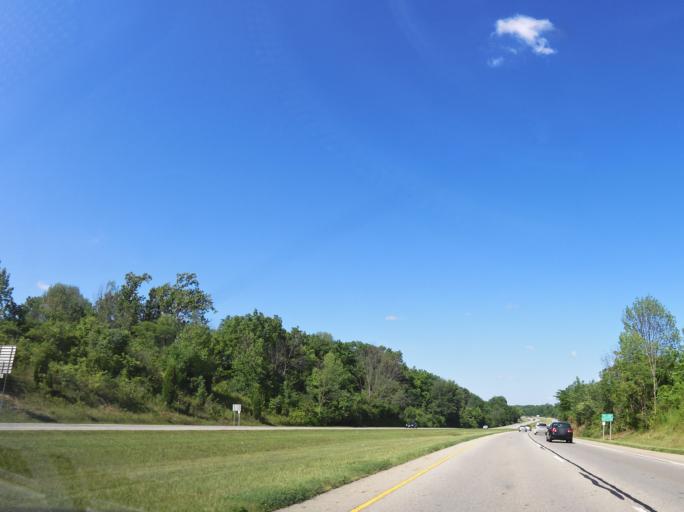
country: US
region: Ohio
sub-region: Greene County
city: Wright-Patterson AFB
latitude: 39.8138
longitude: -84.0841
